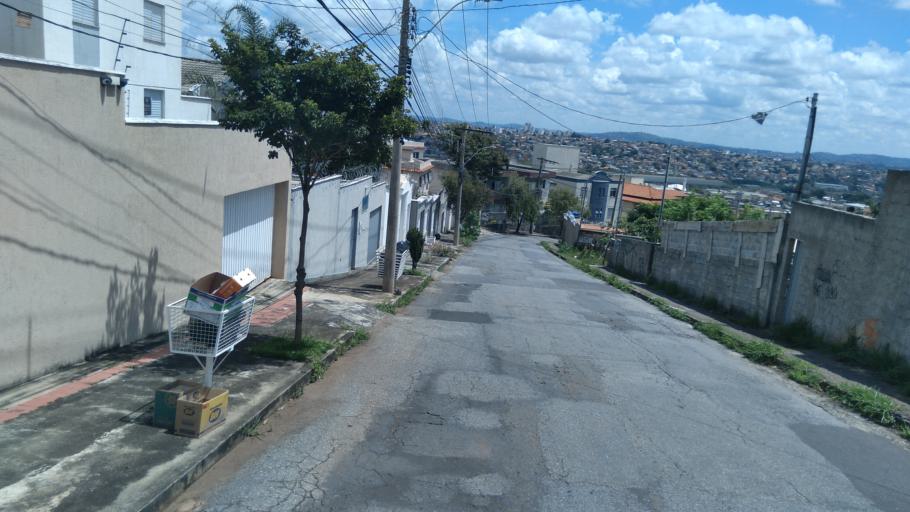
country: BR
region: Minas Gerais
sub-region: Belo Horizonte
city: Belo Horizonte
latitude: -19.8687
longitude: -43.9166
